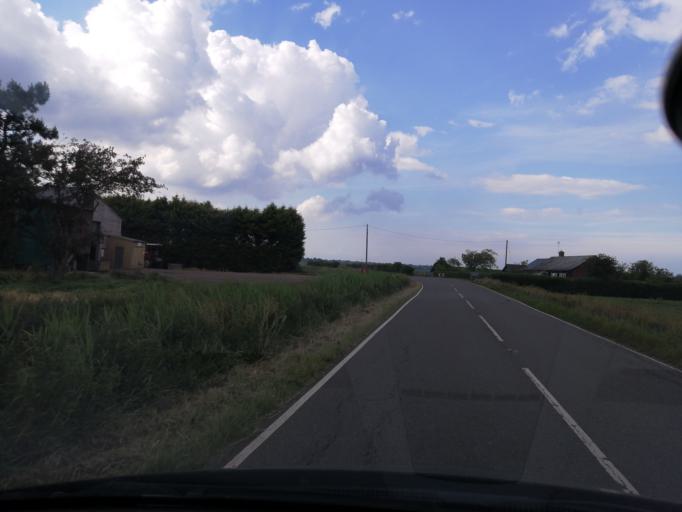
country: GB
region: England
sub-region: Cambridgeshire
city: Yaxley
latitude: 52.4926
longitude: -0.2435
